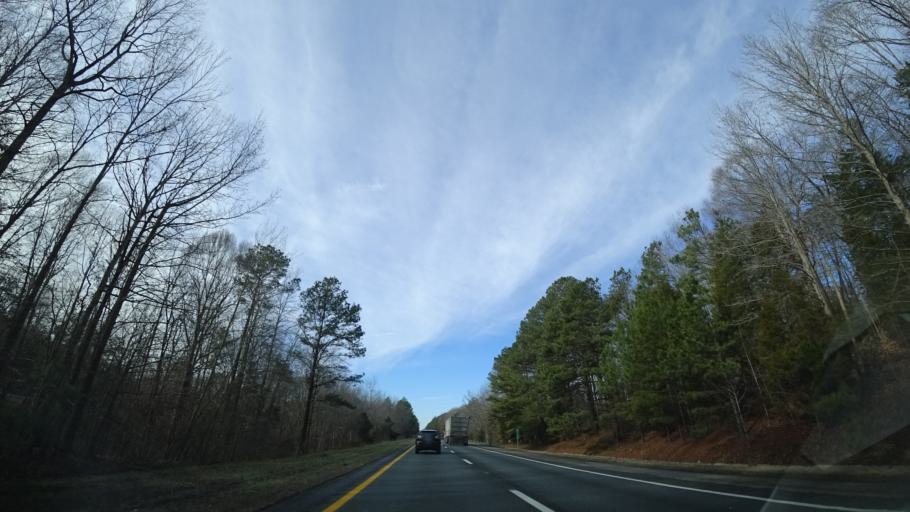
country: US
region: Virginia
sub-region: New Kent County
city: New Kent
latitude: 37.4860
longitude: -76.9640
